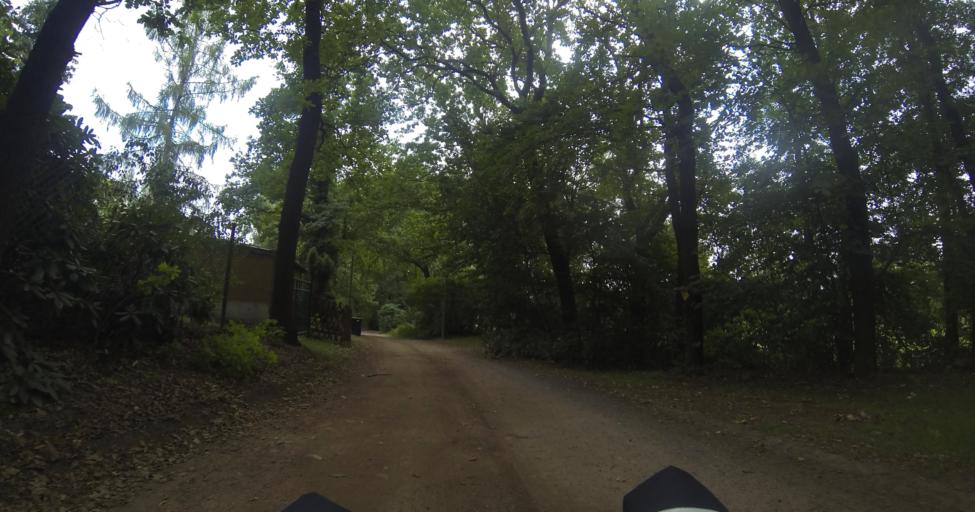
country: DE
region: Saxony
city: Radebeul
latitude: 51.1292
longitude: 13.6346
